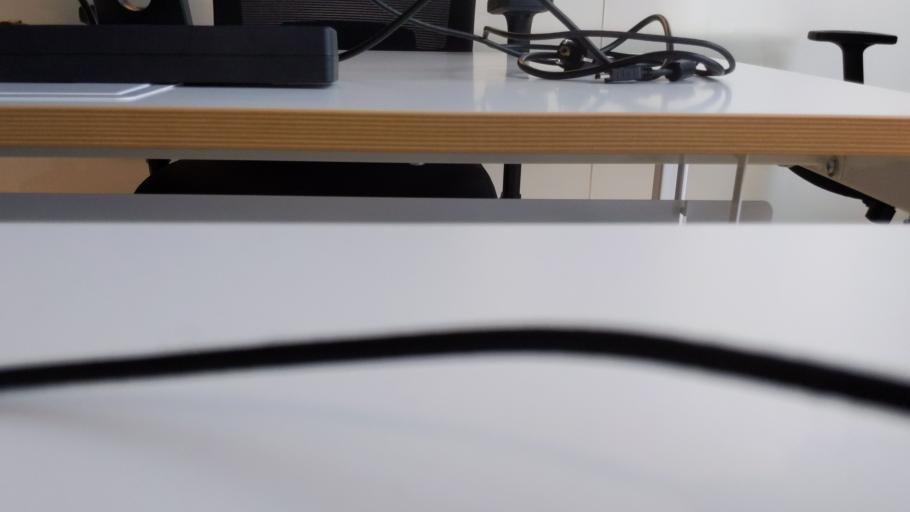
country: RU
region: Moskovskaya
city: Shevlyakovo
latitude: 56.3907
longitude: 36.8629
